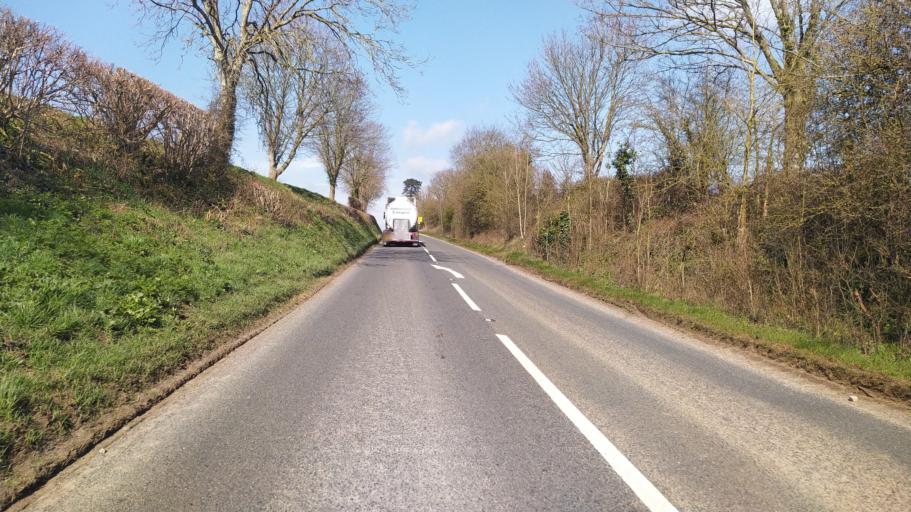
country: GB
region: England
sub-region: Somerset
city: Stoke-sub-Hamdon
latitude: 50.9454
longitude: -2.7688
